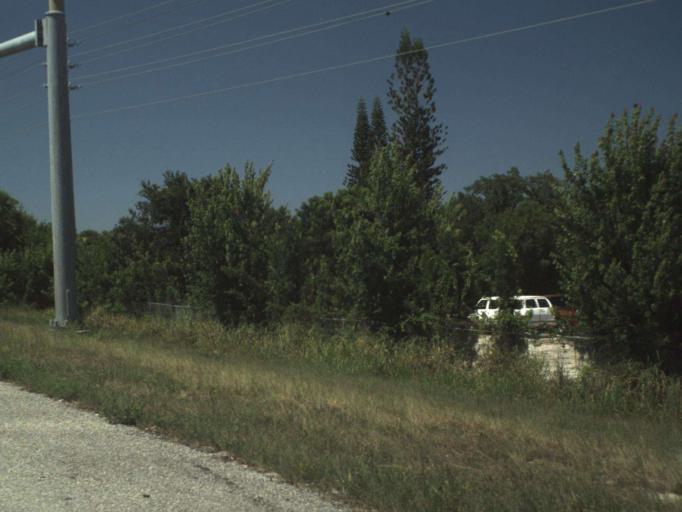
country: US
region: Florida
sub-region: Saint Lucie County
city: Fort Pierce North
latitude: 27.4981
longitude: -80.3452
